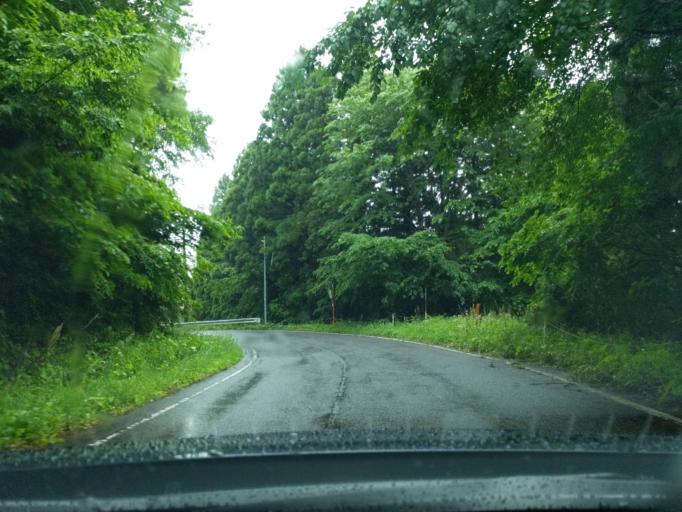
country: JP
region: Fukushima
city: Nihommatsu
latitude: 37.5968
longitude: 140.5719
